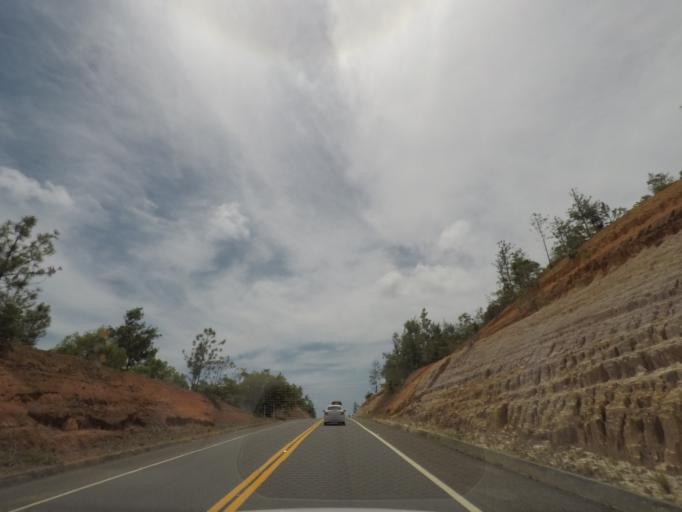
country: BR
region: Bahia
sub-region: Conde
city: Conde
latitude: -11.9808
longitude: -37.6761
